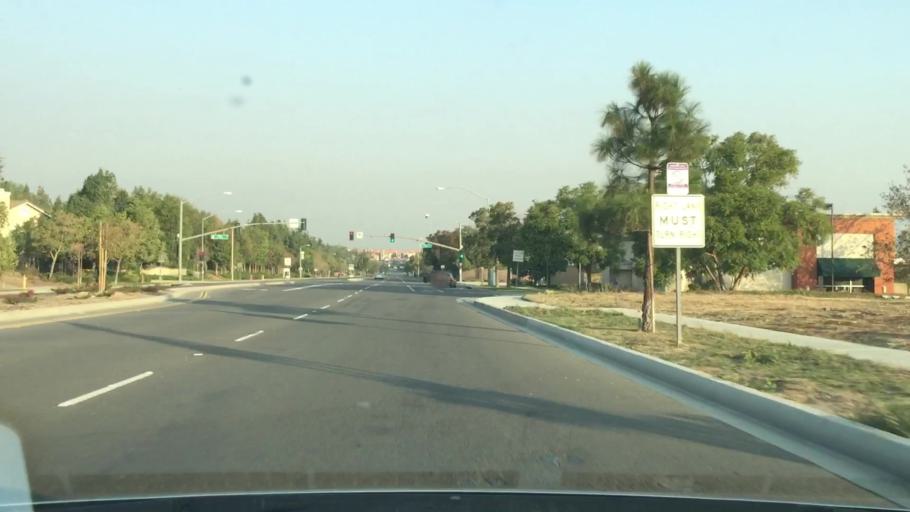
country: US
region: California
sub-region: San Bernardino County
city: Los Serranos
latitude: 33.9461
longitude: -117.6796
